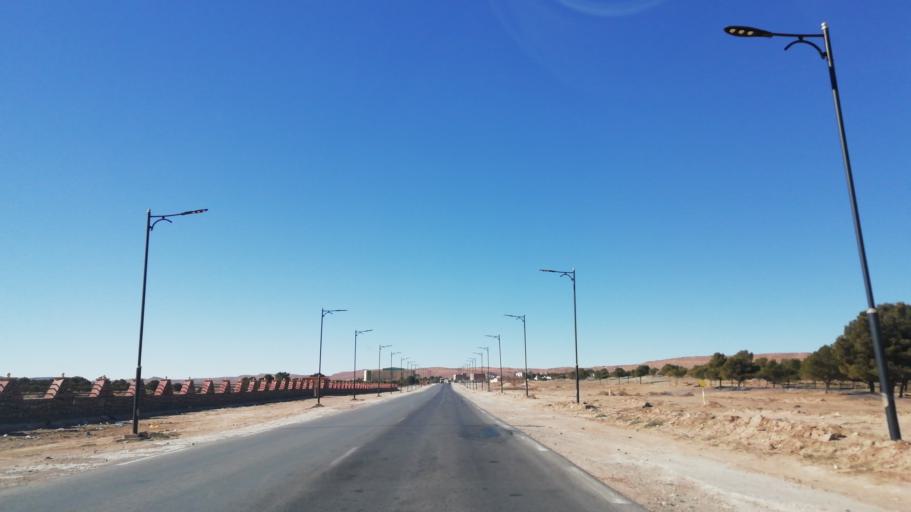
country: DZ
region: El Bayadh
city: El Bayadh
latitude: 33.7293
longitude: 1.5468
